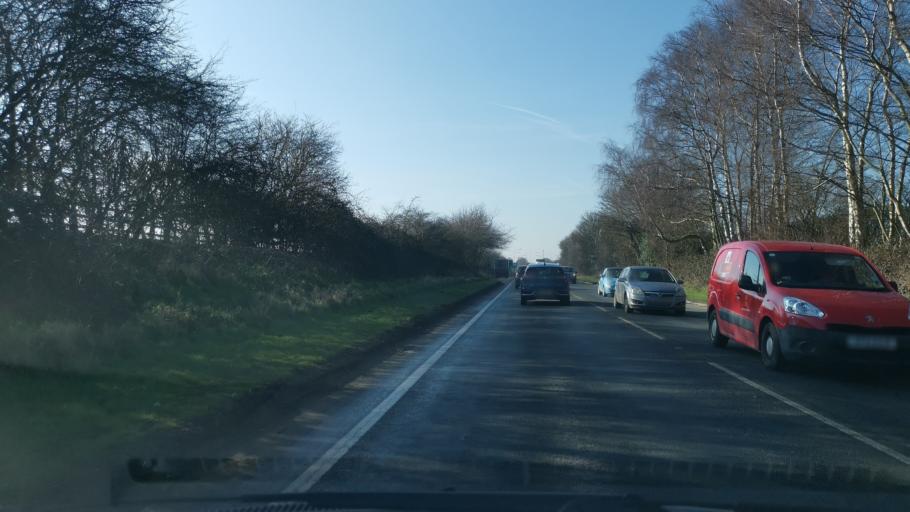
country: GB
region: England
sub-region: City of York
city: Haxby
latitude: 54.0029
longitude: -1.0669
